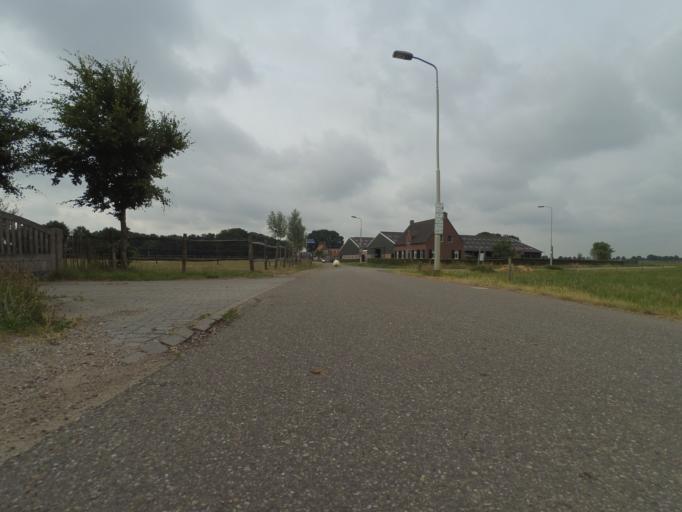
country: BE
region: Flanders
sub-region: Provincie Antwerpen
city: Essen
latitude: 51.4820
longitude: 4.4554
